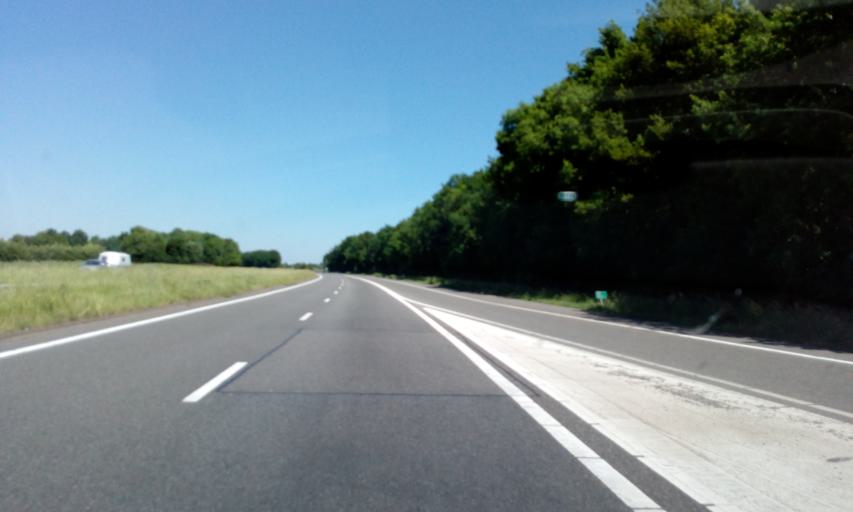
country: NL
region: Limburg
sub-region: Eijsden-Margraten
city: Eijsden
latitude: 50.7789
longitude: 5.7295
